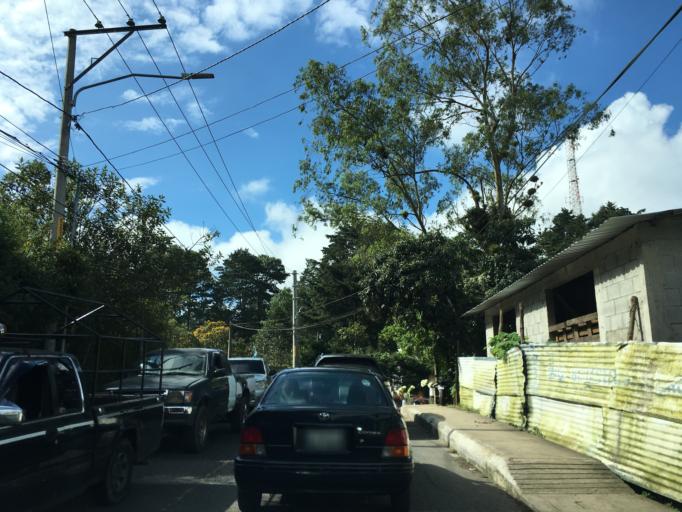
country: GT
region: Guatemala
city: San Jose Pinula
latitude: 14.5654
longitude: -90.4395
